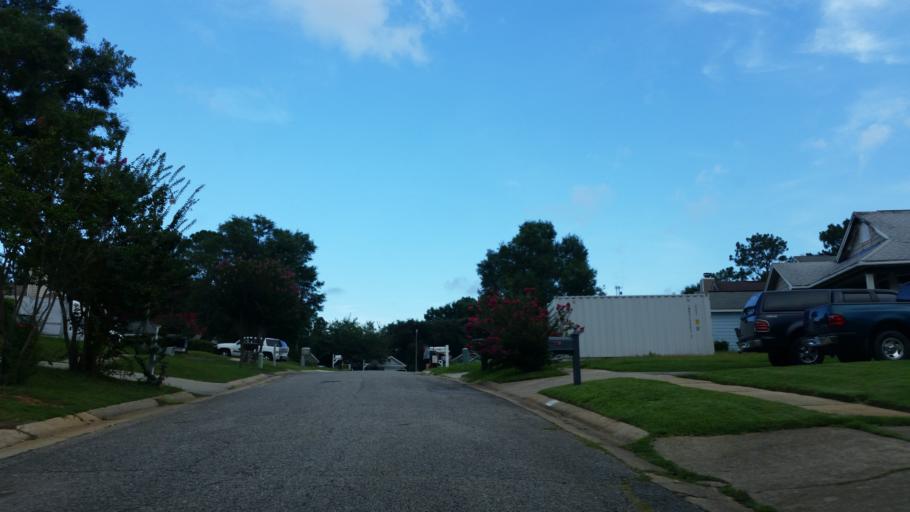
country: US
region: Florida
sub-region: Escambia County
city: Ferry Pass
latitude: 30.5060
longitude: -87.1755
